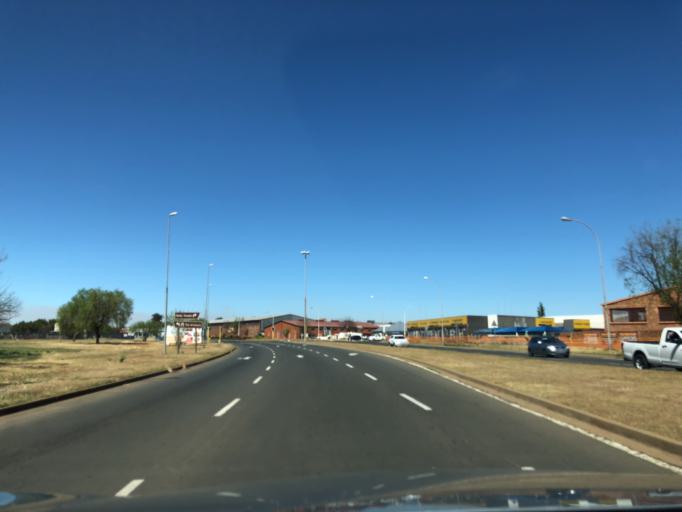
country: ZA
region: KwaZulu-Natal
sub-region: Amajuba District Municipality
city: Newcastle
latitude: -27.7497
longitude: 29.9377
